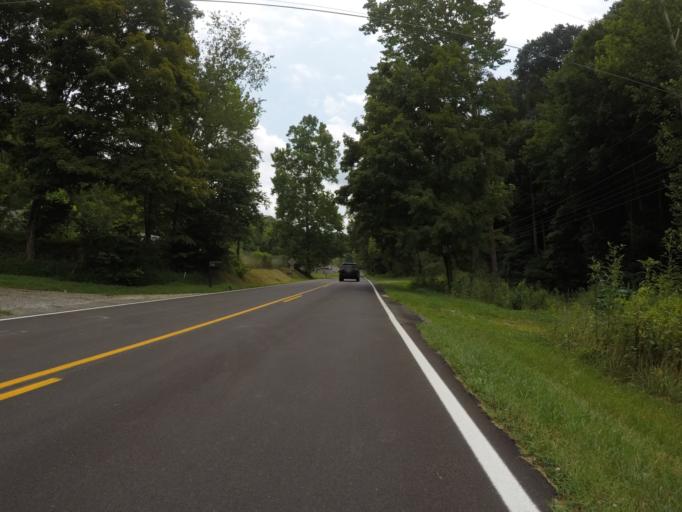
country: US
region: Kentucky
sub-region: Boyd County
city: Catlettsburg
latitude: 38.4221
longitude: -82.6257
